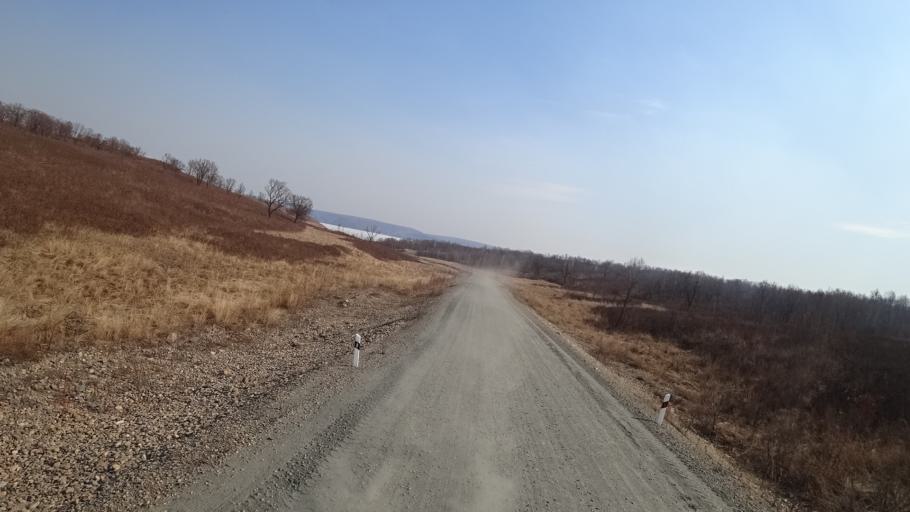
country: RU
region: Amur
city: Novobureyskiy
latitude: 49.8247
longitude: 129.9957
